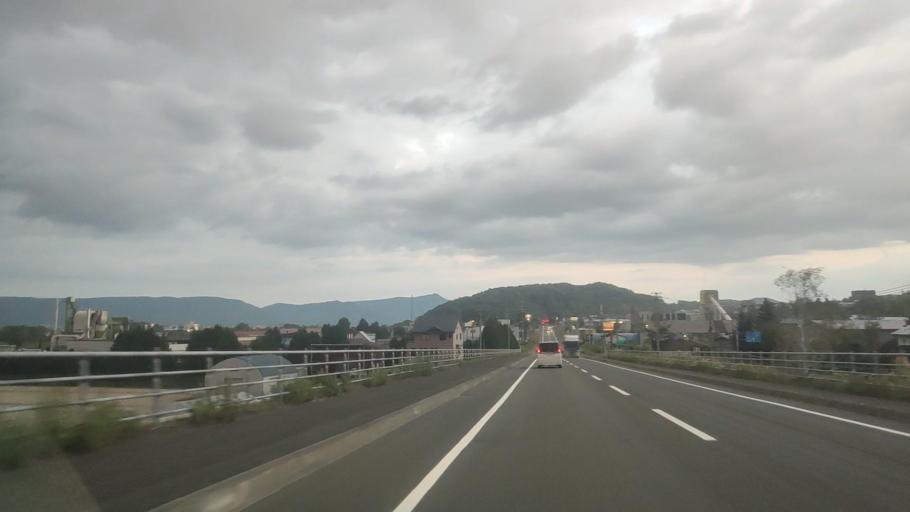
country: JP
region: Hokkaido
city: Shimo-furano
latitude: 43.3527
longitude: 142.3657
